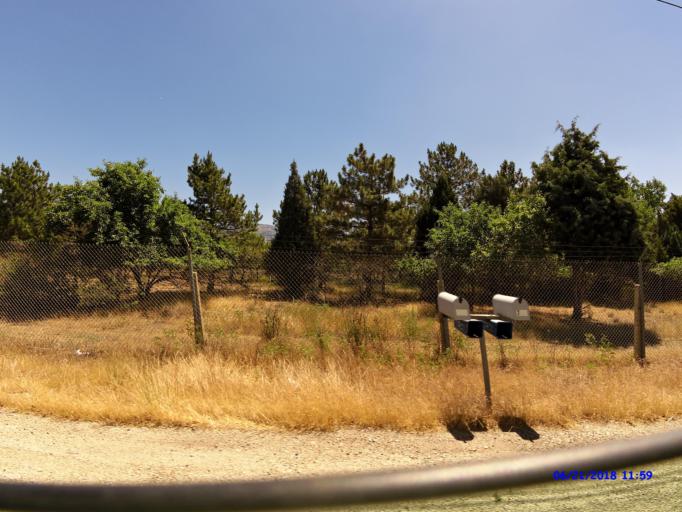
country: US
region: Utah
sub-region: Weber County
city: Marriott-Slaterville
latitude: 41.2504
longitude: -112.0096
